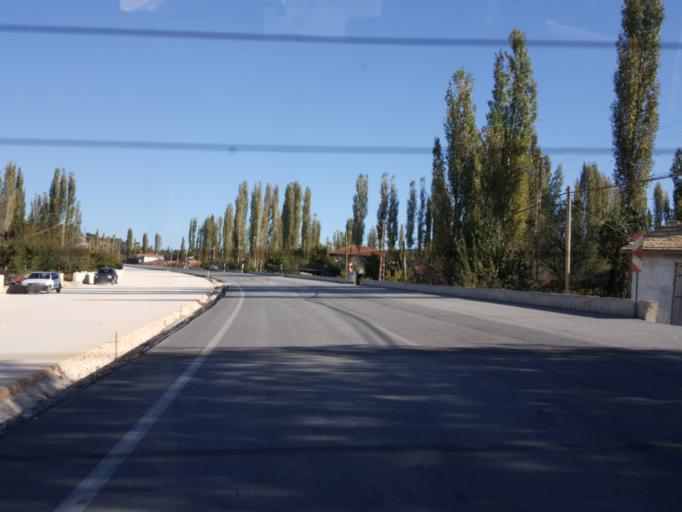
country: TR
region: Amasya
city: Ezinepazari
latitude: 40.5449
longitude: 36.1519
